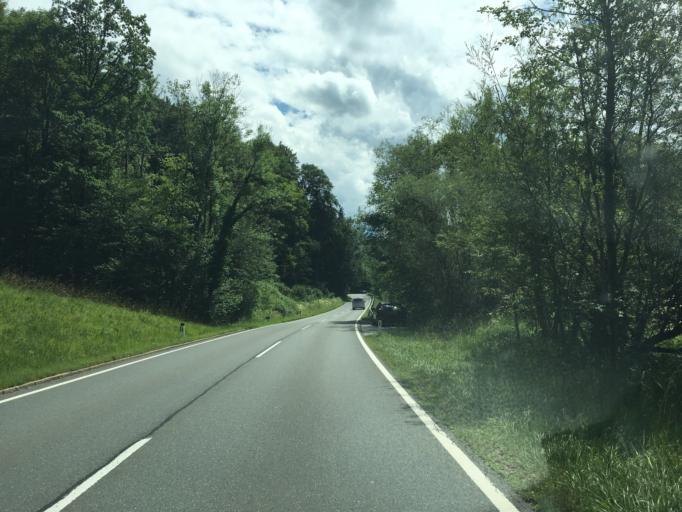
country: AT
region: Salzburg
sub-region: Politischer Bezirk Hallein
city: Adnet
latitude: 47.7183
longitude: 13.1364
